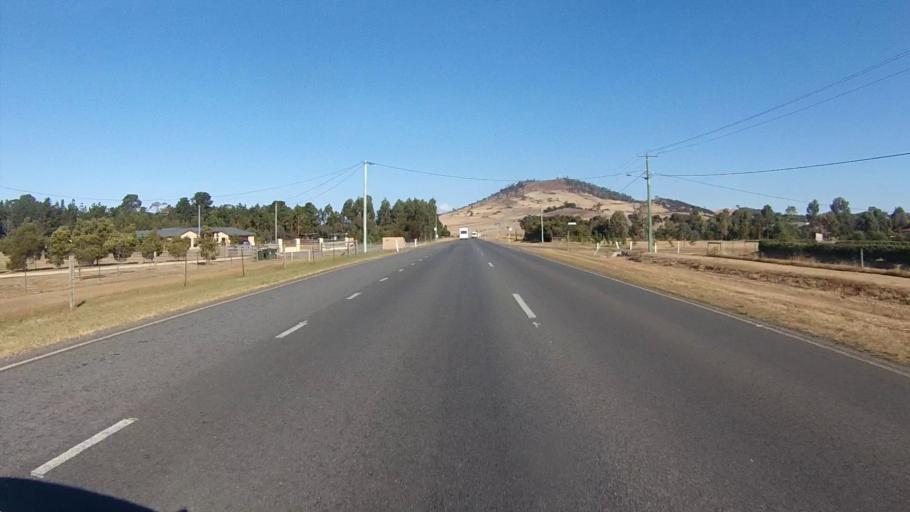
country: AU
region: Tasmania
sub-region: Clarence
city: Seven Mile Beach
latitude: -42.8574
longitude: 147.4907
